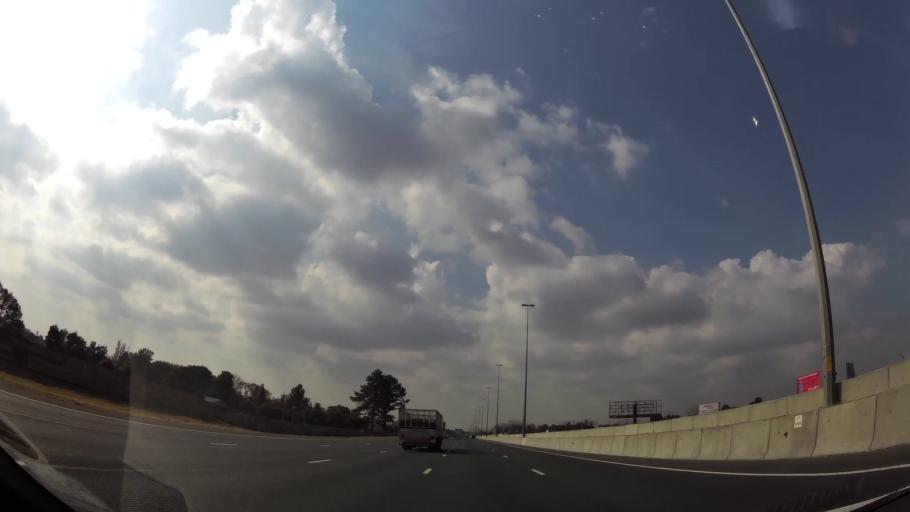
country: ZA
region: Gauteng
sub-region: Ekurhuleni Metropolitan Municipality
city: Boksburg
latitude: -26.1726
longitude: 28.2557
